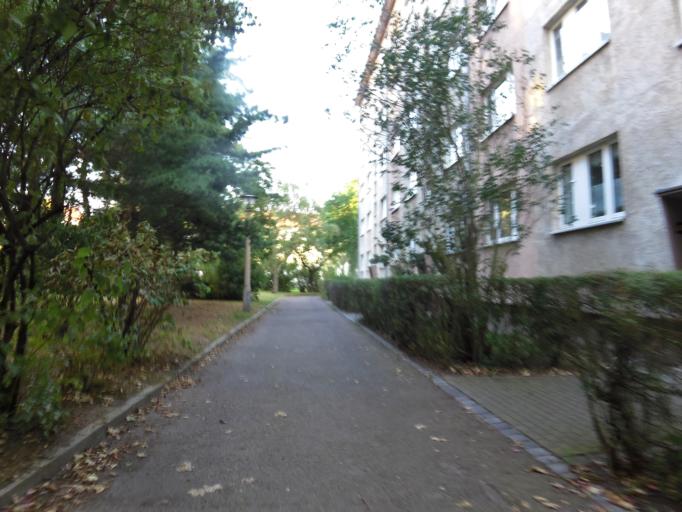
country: DE
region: Saxony
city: Leipzig
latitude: 51.3340
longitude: 12.3095
